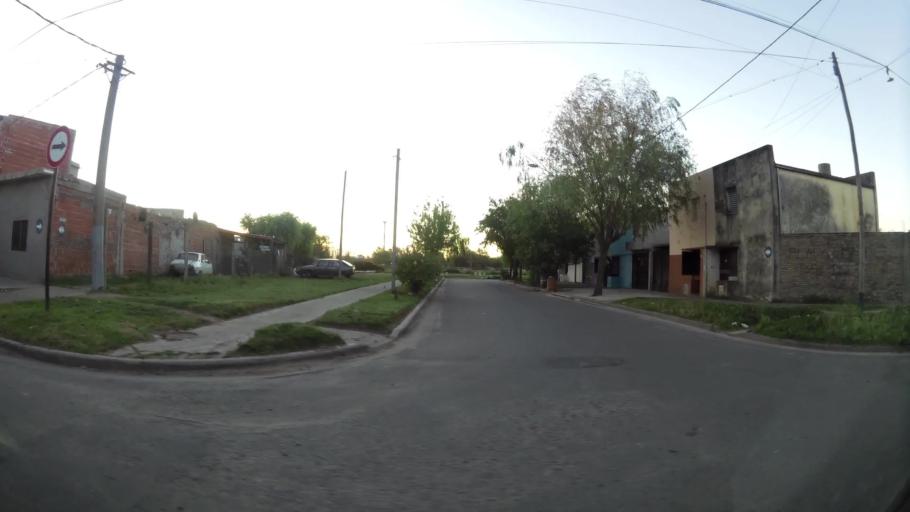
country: AR
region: Santa Fe
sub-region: Departamento de Rosario
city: Rosario
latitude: -32.9704
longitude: -60.6884
